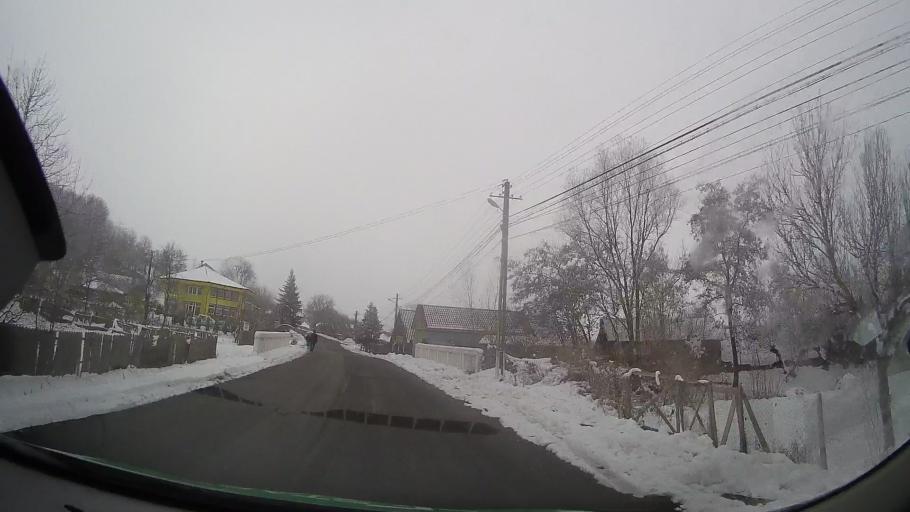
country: RO
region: Bacau
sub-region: Comuna Oncesti
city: Oncesti
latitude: 46.4723
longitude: 27.2555
